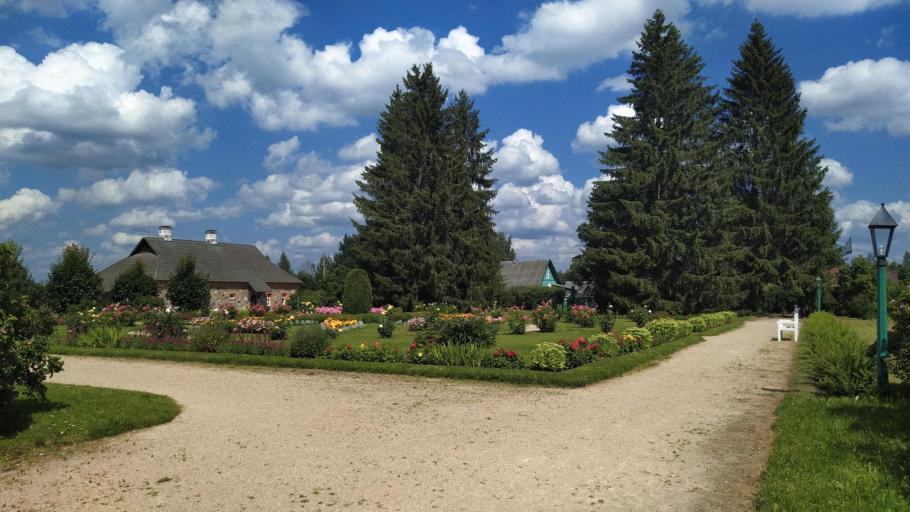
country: RU
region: Pskov
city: Pushkinskiye Gory
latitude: 57.0787
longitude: 28.9504
